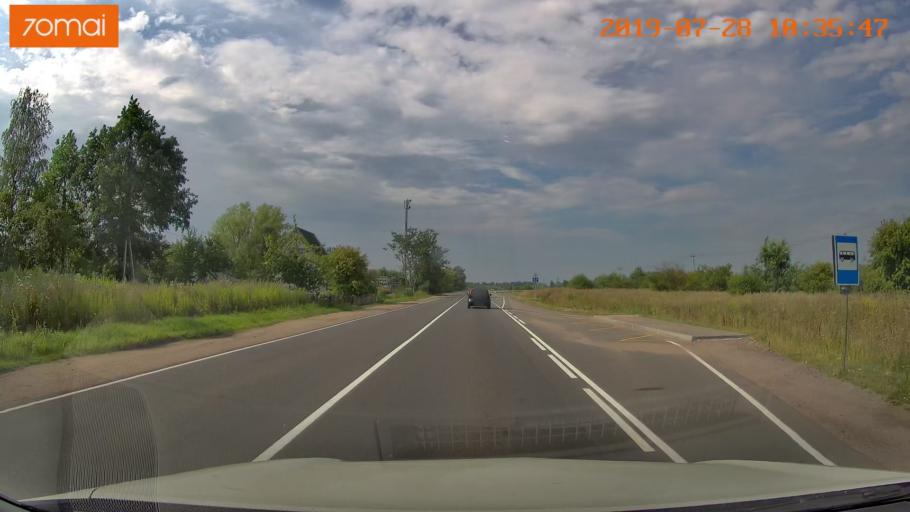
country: RU
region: Kaliningrad
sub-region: Gorod Kaliningrad
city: Kaliningrad
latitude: 54.7434
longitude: 20.4281
